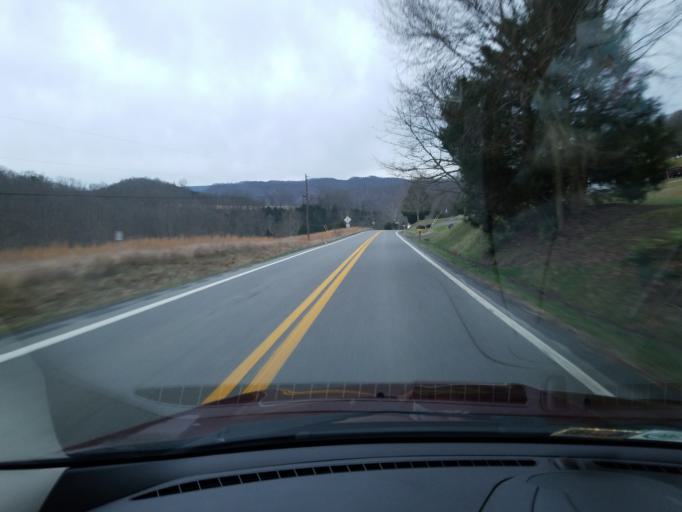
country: US
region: West Virginia
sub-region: Monroe County
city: Union
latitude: 37.5663
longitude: -80.5687
